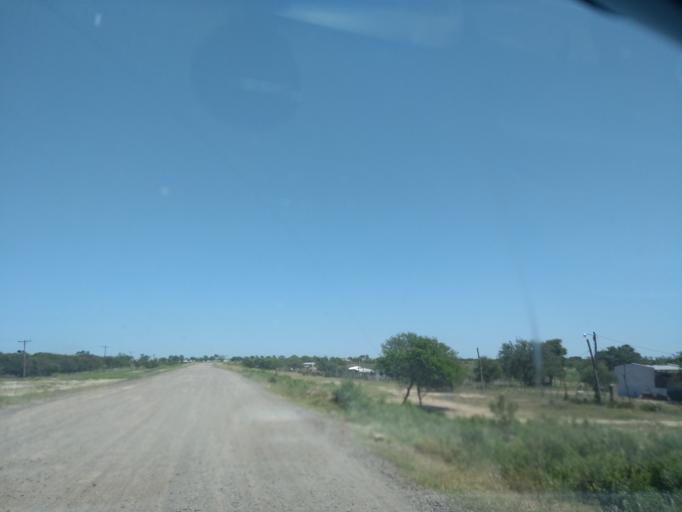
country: AR
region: Chaco
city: Resistencia
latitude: -27.4082
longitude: -58.9531
